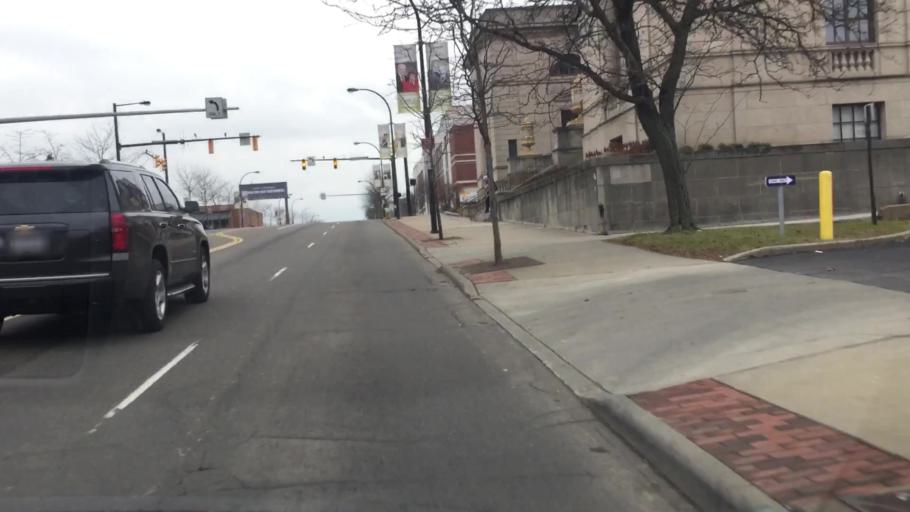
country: US
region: Ohio
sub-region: Summit County
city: Akron
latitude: 41.0836
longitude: -81.5127
